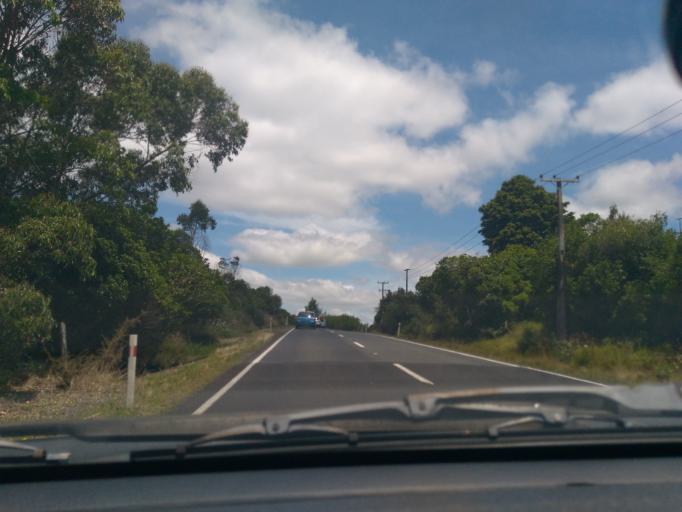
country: NZ
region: Northland
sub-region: Far North District
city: Kerikeri
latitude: -35.1465
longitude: 173.8824
